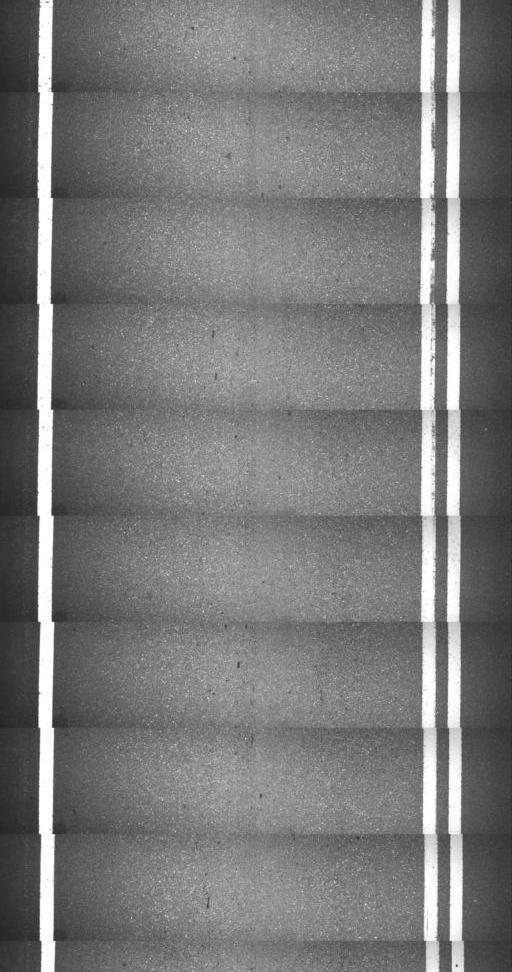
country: US
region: Vermont
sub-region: Windham County
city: Bellows Falls
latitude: 43.1214
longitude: -72.4371
